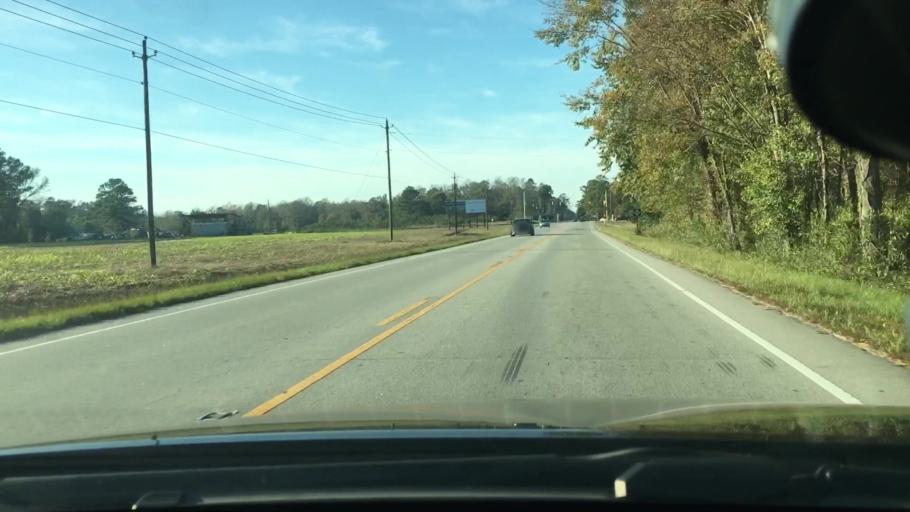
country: US
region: North Carolina
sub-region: Craven County
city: Vanceboro
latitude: 35.2477
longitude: -77.0867
